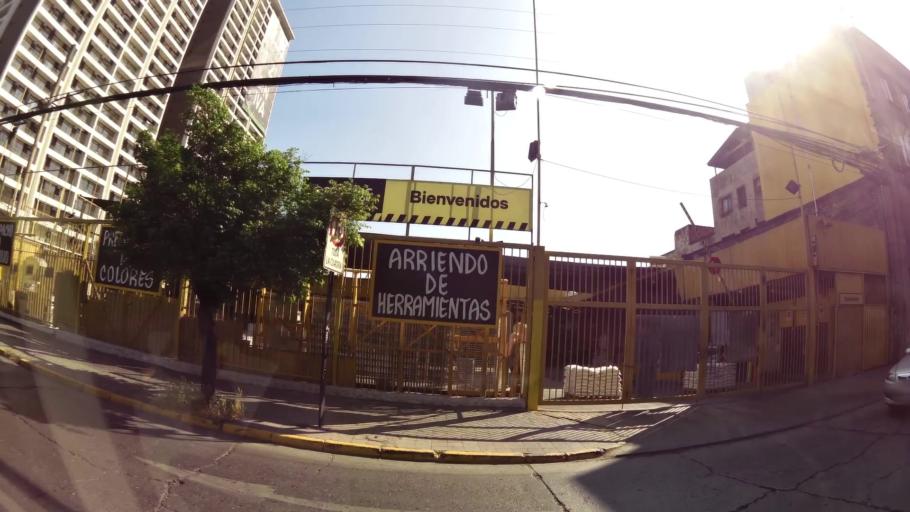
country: CL
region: Santiago Metropolitan
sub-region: Provincia de Santiago
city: Santiago
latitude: -33.4505
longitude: -70.6296
